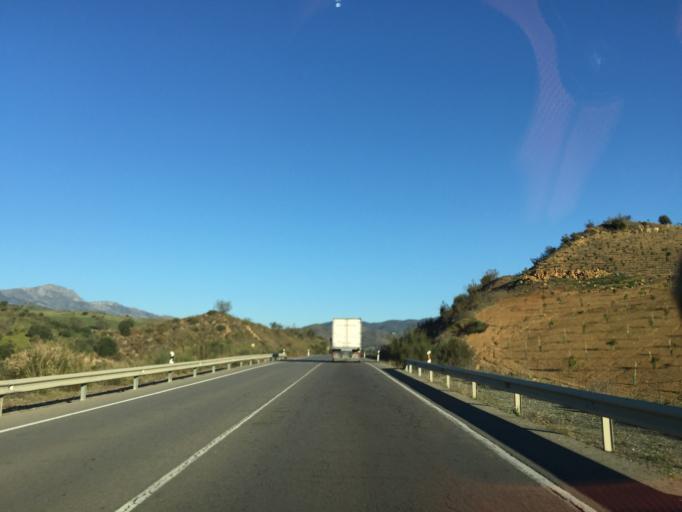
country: ES
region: Andalusia
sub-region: Provincia de Malaga
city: Pizarra
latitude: 36.7810
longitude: -4.7423
